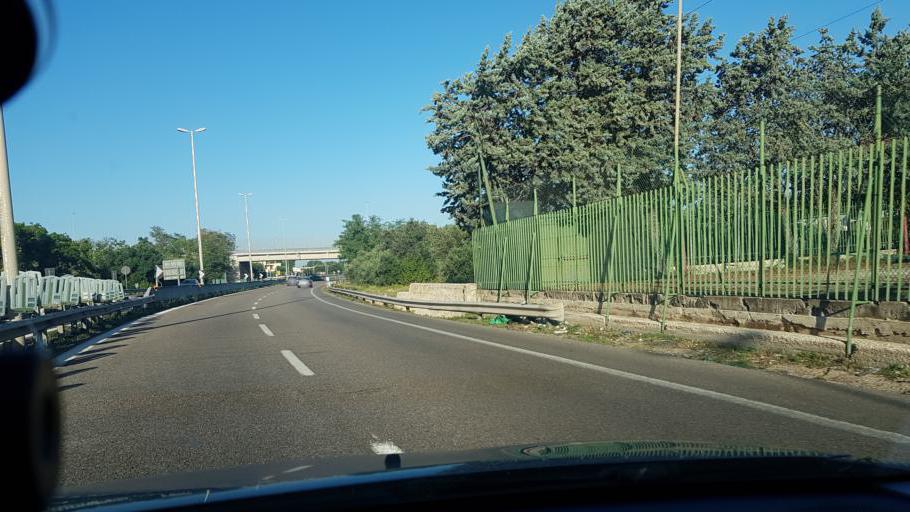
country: IT
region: Apulia
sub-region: Provincia di Bari
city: Parco Scizzo-Parchitello
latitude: 41.0840
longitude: 16.9952
